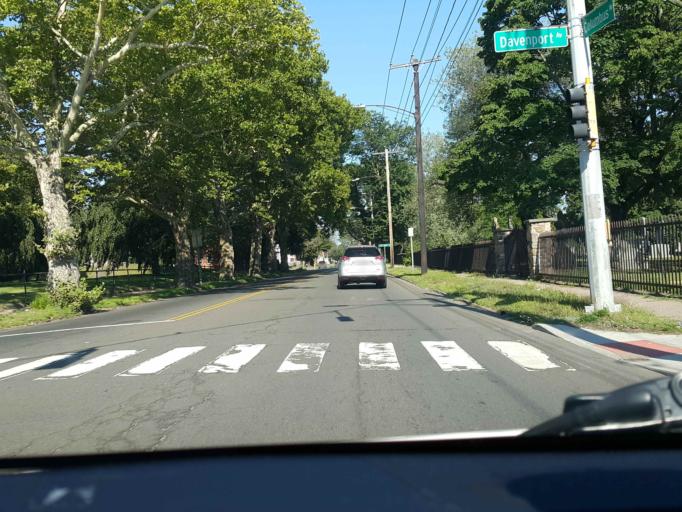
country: US
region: Connecticut
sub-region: New Haven County
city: New Haven
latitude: 41.2975
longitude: -72.9479
